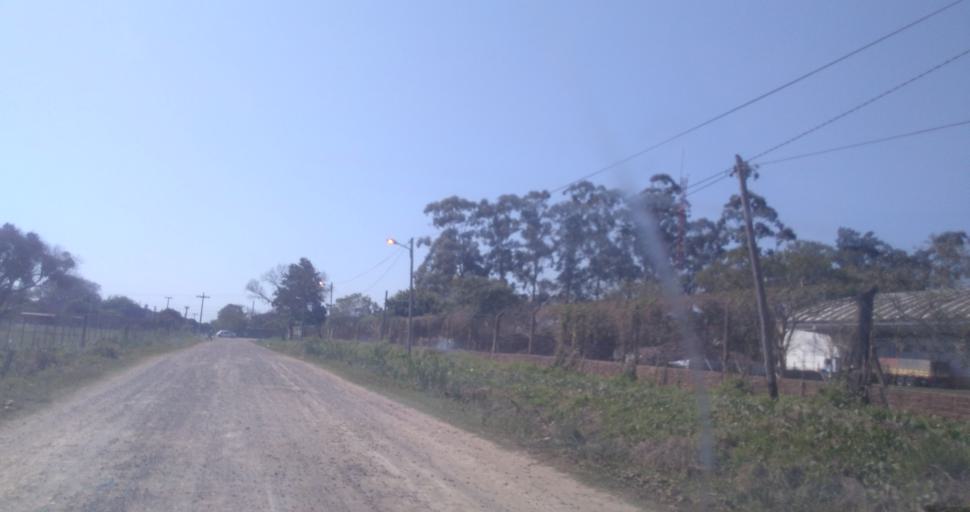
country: AR
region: Chaco
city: Fontana
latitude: -27.4292
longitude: -59.0285
